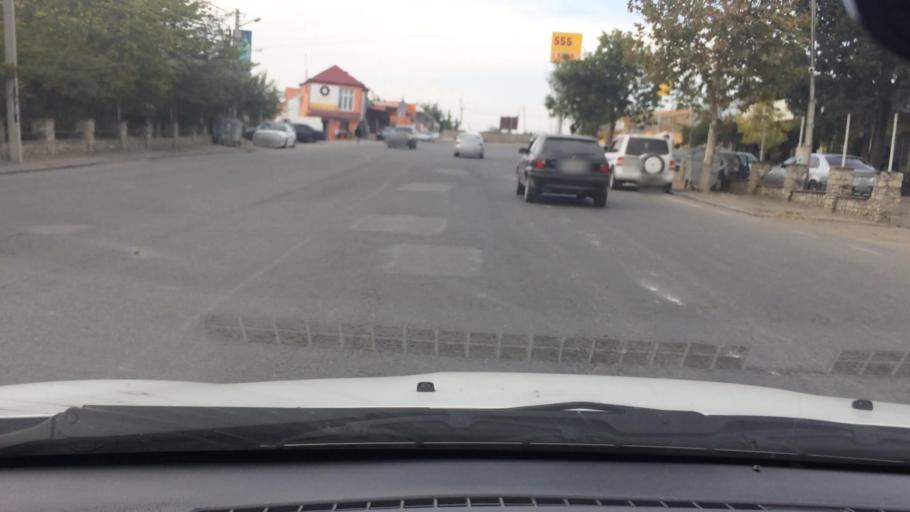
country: GE
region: Kvemo Kartli
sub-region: Marneuli
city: Marneuli
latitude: 41.4934
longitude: 44.8023
